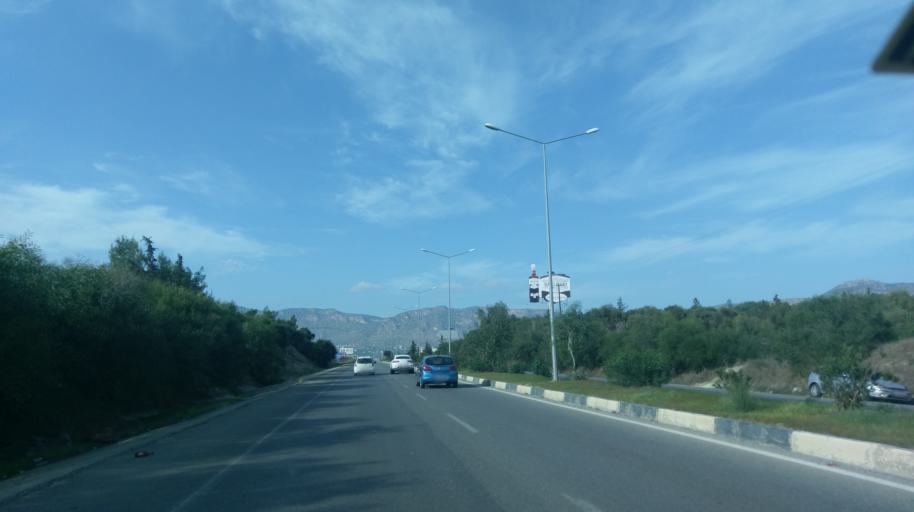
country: CY
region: Keryneia
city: Kyrenia
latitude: 35.2504
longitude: 33.3037
